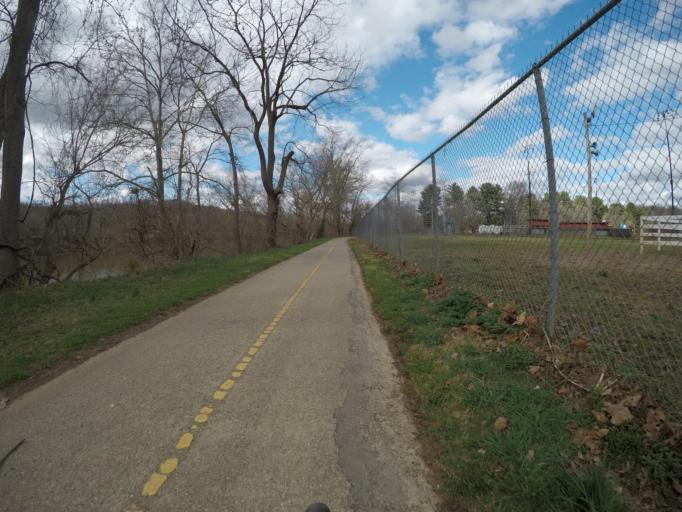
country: US
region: Ohio
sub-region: Washington County
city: Marietta
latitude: 39.4307
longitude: -81.4722
